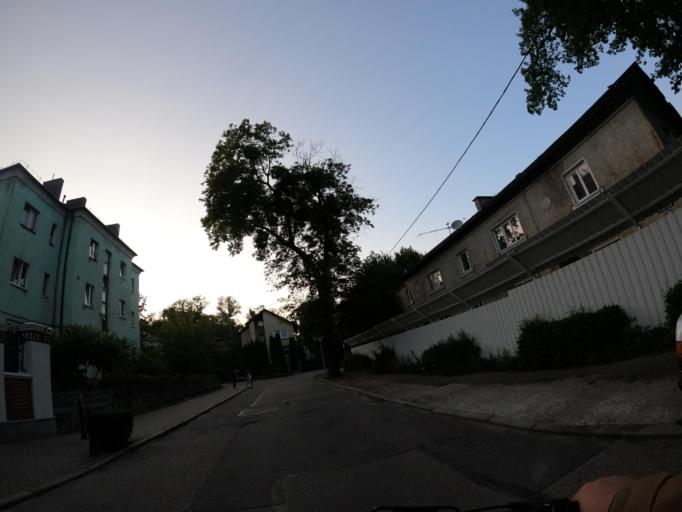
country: RU
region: Kaliningrad
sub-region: Gorod Kaliningrad
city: Kaliningrad
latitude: 54.7200
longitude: 20.4686
